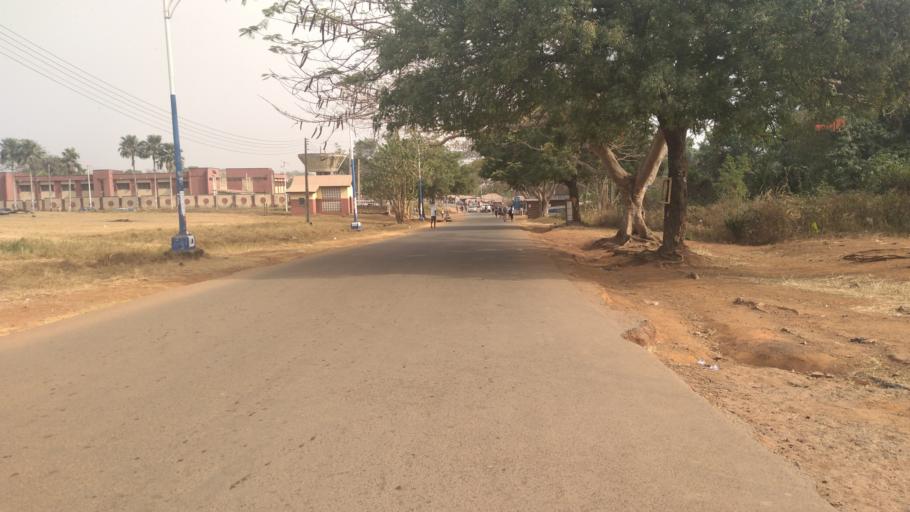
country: NG
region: Ondo
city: Ilare
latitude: 7.3044
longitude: 5.1402
